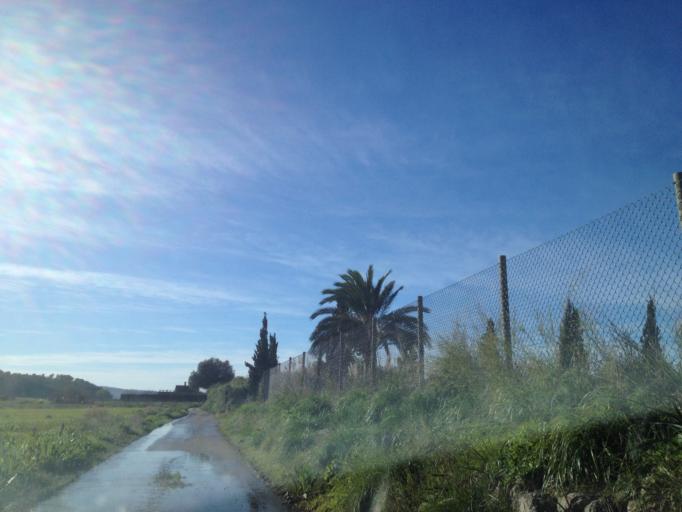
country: ES
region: Balearic Islands
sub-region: Illes Balears
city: Sineu
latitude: 39.6491
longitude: 3.0363
